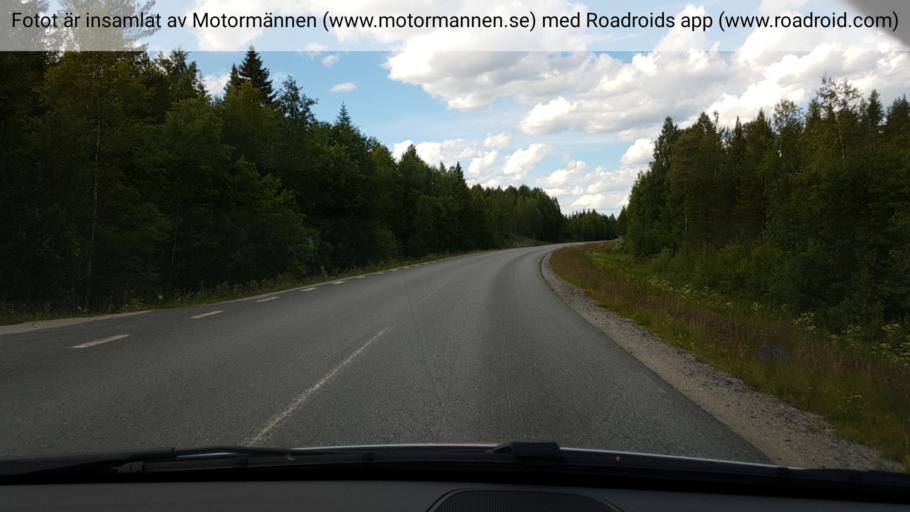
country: SE
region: Jaemtland
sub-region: Braecke Kommun
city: Braecke
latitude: 62.4049
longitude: 15.0171
